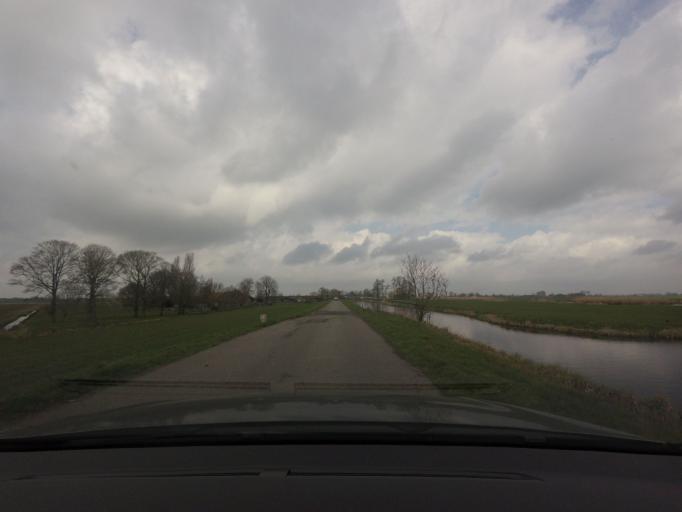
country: NL
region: North Holland
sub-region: Gemeente Uithoorn
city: Uithoorn
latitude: 52.1930
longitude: 4.8122
